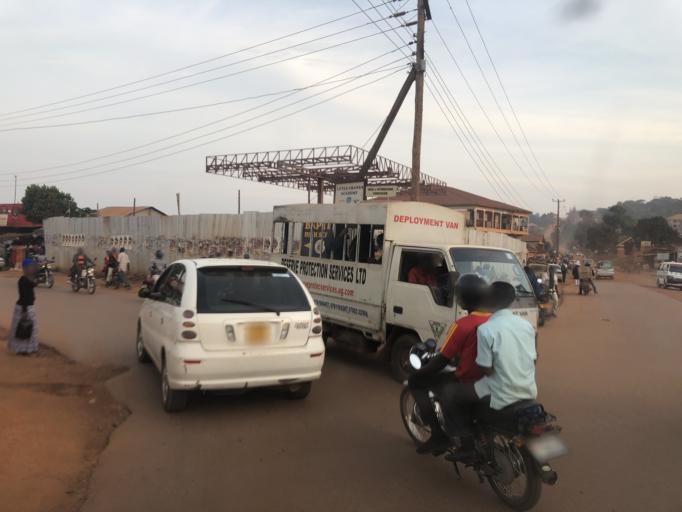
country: UG
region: Central Region
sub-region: Kampala District
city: Kampala
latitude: 0.2736
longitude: 32.5466
